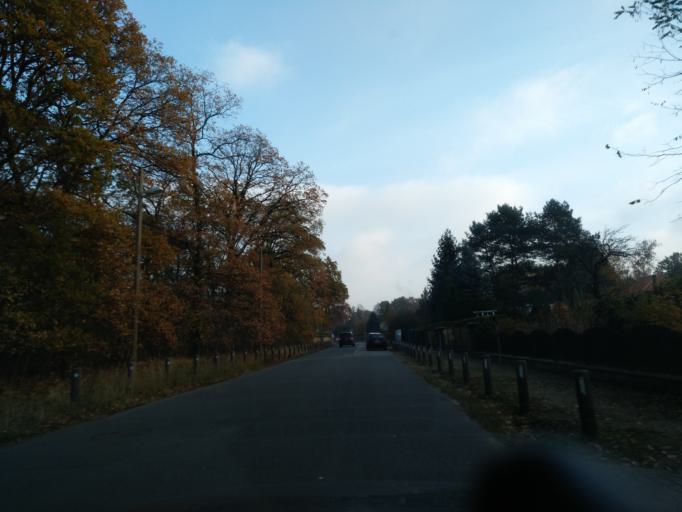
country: DE
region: Berlin
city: Staaken
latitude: 52.5664
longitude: 13.1377
